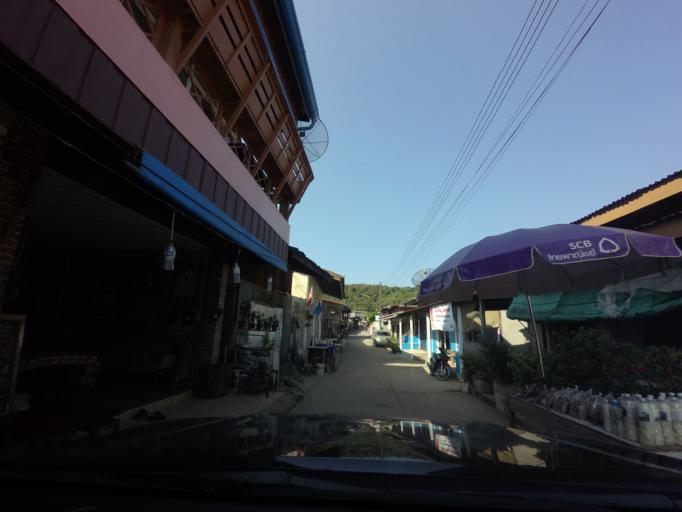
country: TH
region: Kanchanaburi
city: Thong Pha Phum
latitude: 14.6794
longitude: 98.3695
